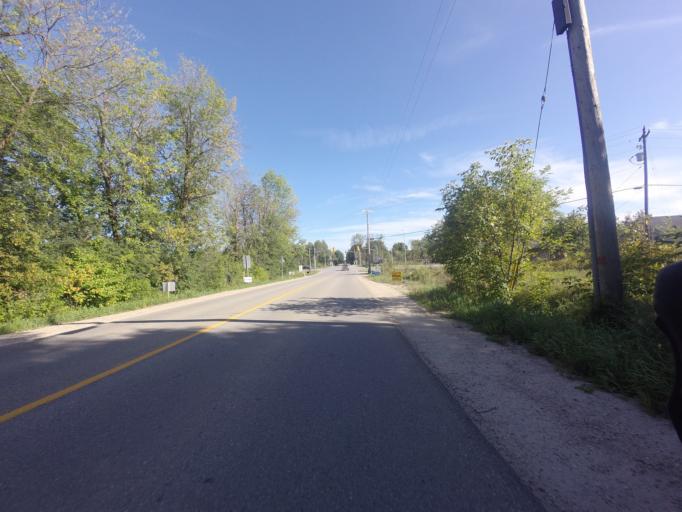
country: CA
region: Ontario
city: Perth
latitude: 44.8861
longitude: -76.3133
